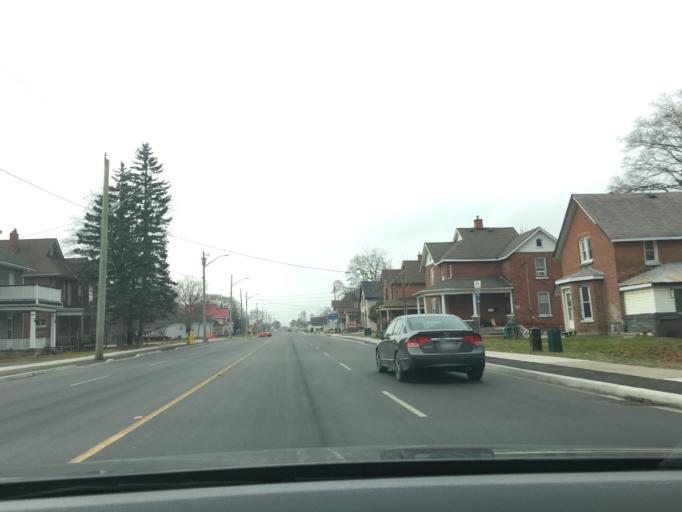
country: CA
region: Ontario
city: Barrie
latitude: 44.3847
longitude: -79.7007
